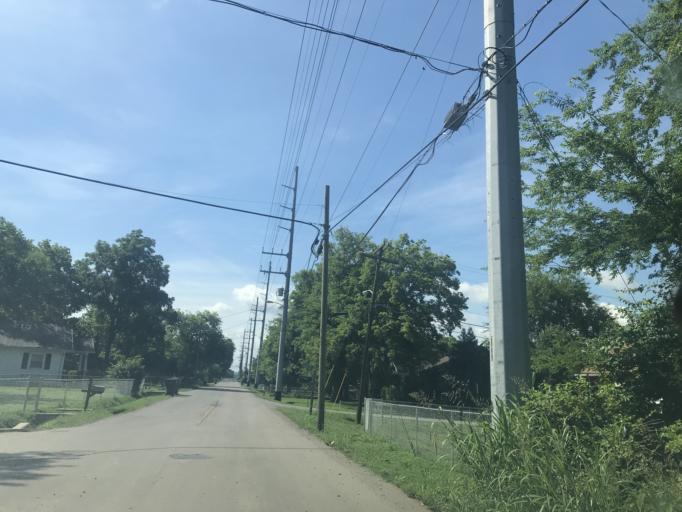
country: US
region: Tennessee
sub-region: Davidson County
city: Nashville
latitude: 36.1934
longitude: -86.8403
